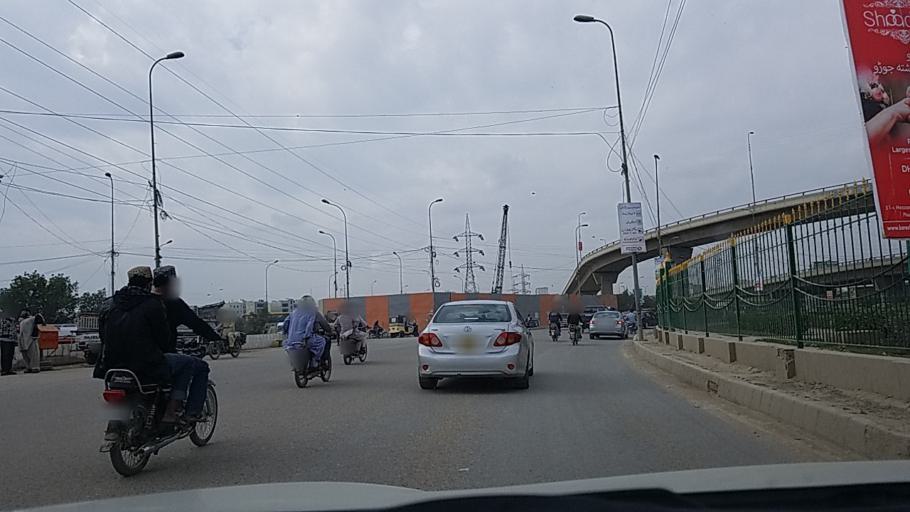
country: PK
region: Sindh
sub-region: Karachi District
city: Karachi
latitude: 24.8297
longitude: 67.0796
